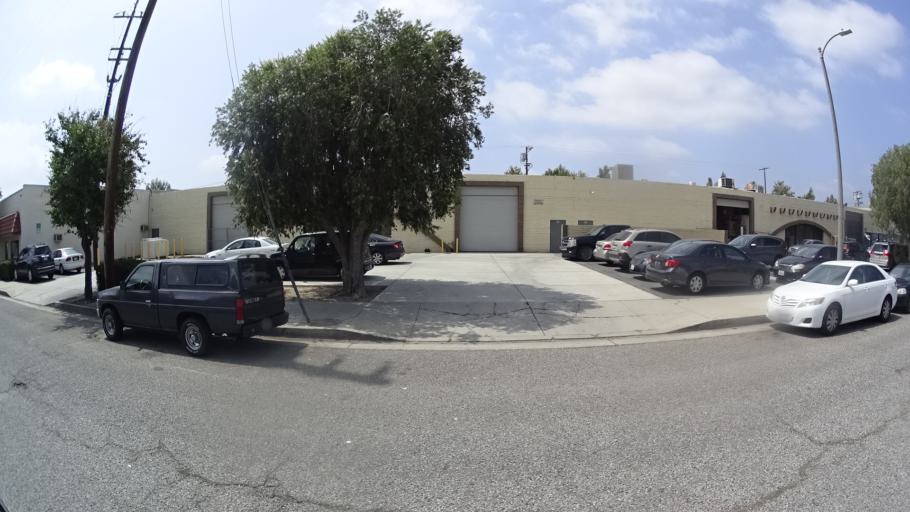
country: US
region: California
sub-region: Los Angeles County
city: Van Nuys
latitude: 34.1812
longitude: -118.4592
